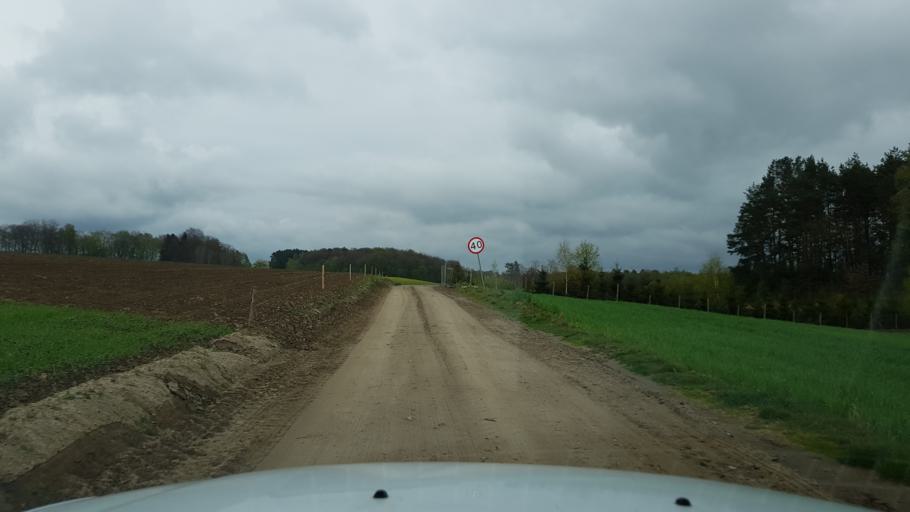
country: PL
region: West Pomeranian Voivodeship
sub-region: Powiat kolobrzeski
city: Ryman
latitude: 54.0319
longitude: 15.4842
